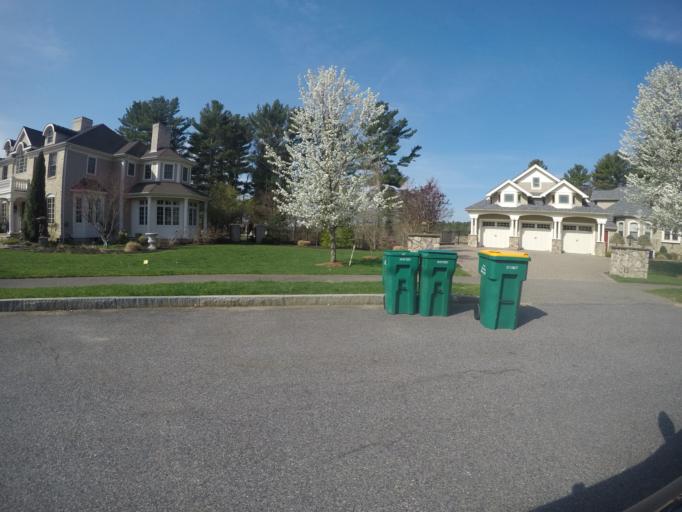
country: US
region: Massachusetts
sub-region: Bristol County
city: Easton
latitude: 42.0002
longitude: -71.1237
